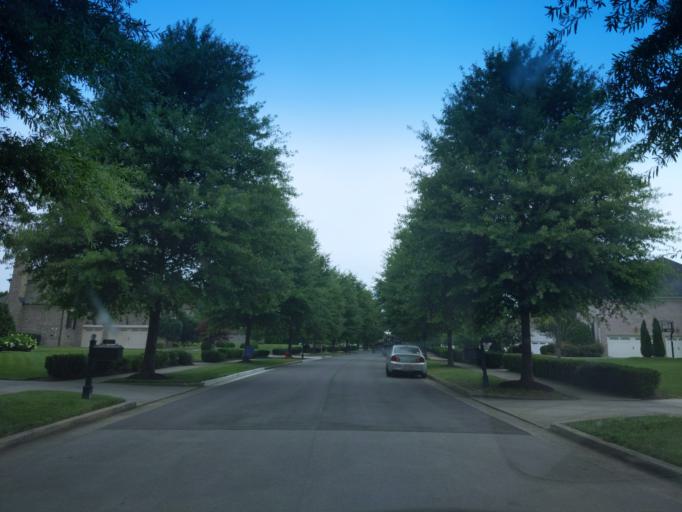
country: US
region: Tennessee
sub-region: Williamson County
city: Brentwood Estates
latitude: 36.0257
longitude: -86.7716
